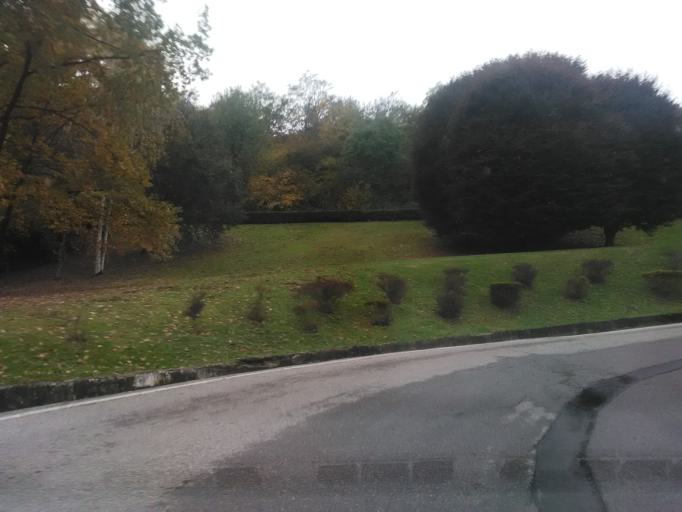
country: IT
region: Piedmont
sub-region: Provincia di Novara
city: Pella
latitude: 45.7932
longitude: 8.3824
